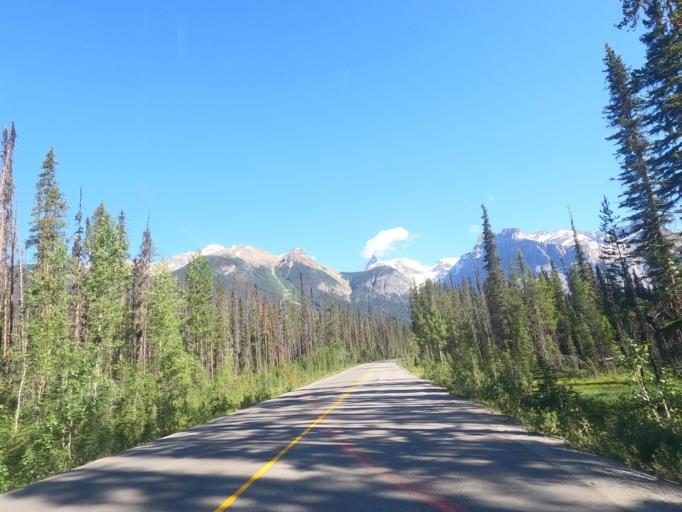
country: CA
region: Alberta
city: Lake Louise
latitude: 51.4242
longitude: -116.5332
